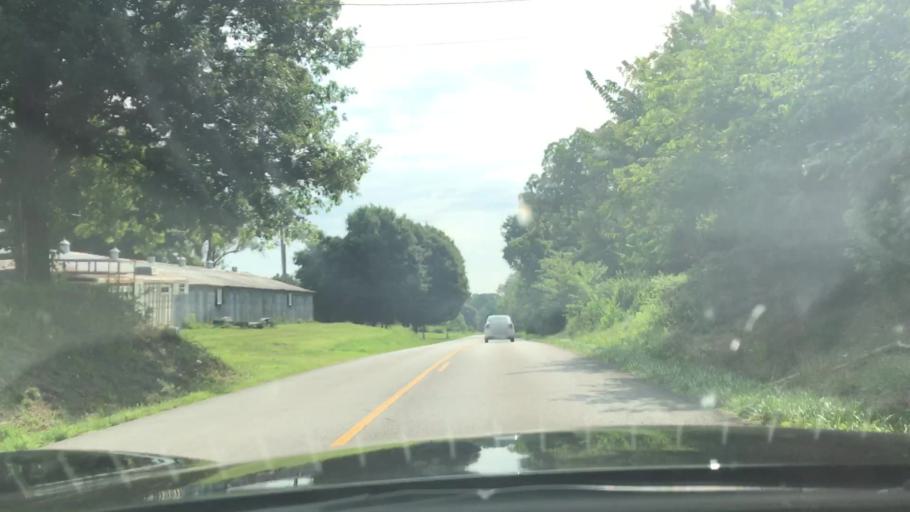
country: US
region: Kentucky
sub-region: Green County
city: Greensburg
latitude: 37.2627
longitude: -85.5522
